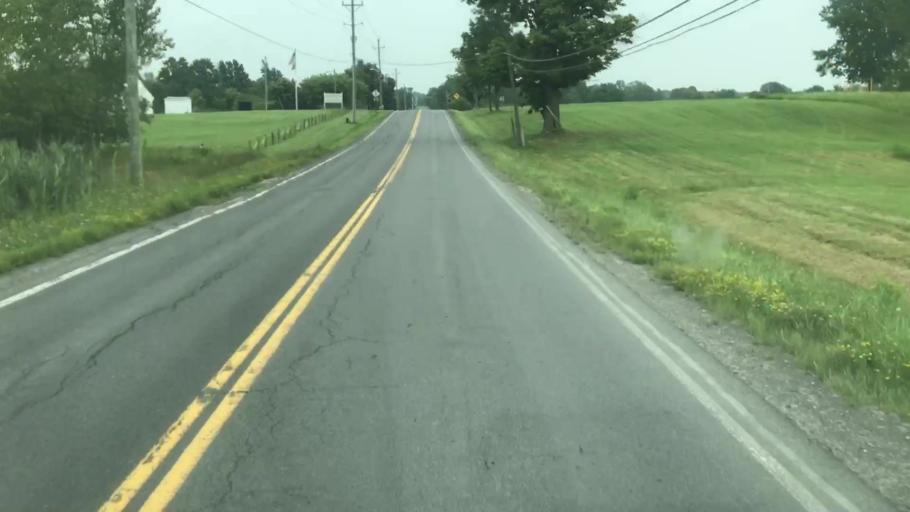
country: US
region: New York
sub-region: Cayuga County
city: Melrose Park
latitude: 42.9532
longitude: -76.5058
